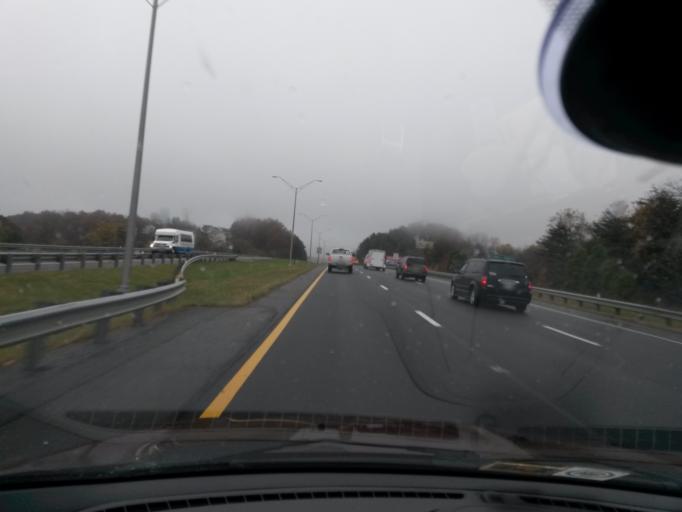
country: US
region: Virginia
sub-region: Montgomery County
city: Christiansburg
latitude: 37.1366
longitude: -80.3779
